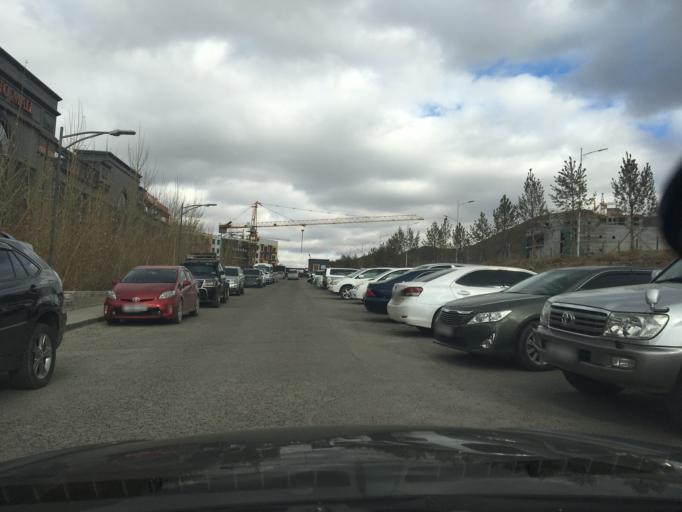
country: MN
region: Ulaanbaatar
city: Ulaanbaatar
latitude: 47.8780
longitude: 106.8513
